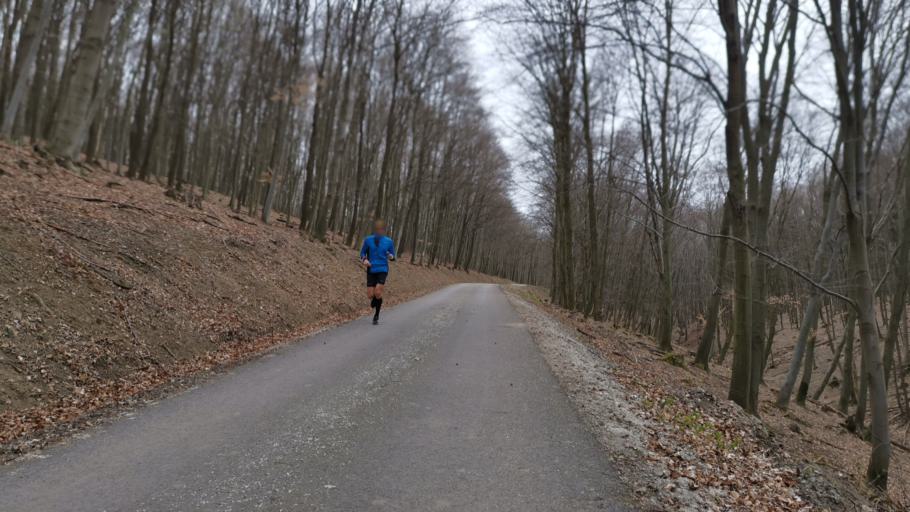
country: CZ
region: South Moravian
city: Petrov
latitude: 48.8123
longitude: 17.3227
